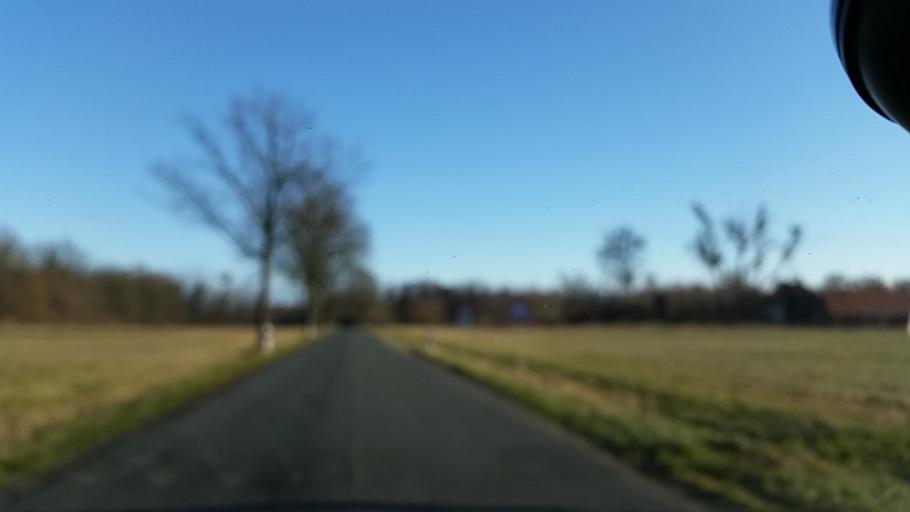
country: DE
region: Lower Saxony
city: Parsau
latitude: 52.5172
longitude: 10.9220
